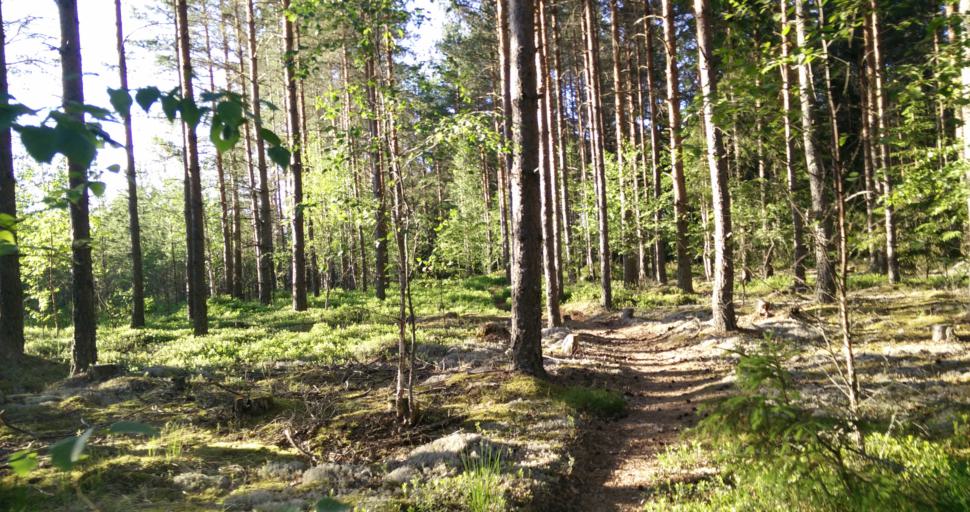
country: SE
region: Vaermland
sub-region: Hagfors Kommun
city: Hagfors
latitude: 60.0198
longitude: 13.5832
